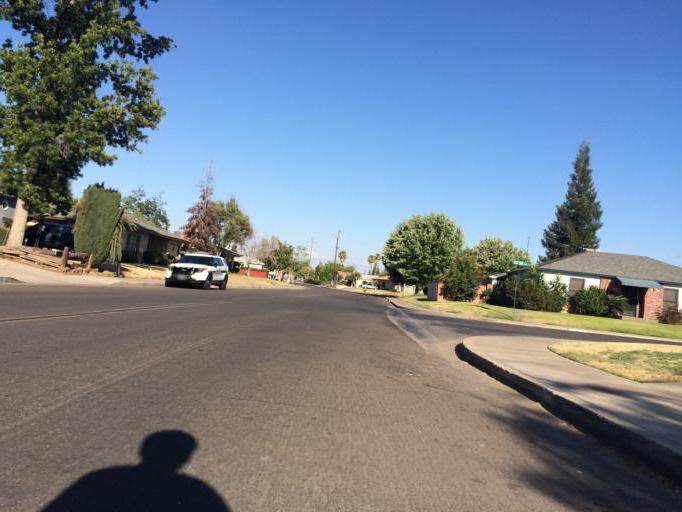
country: US
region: California
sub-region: Fresno County
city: Fresno
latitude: 36.7690
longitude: -119.7666
